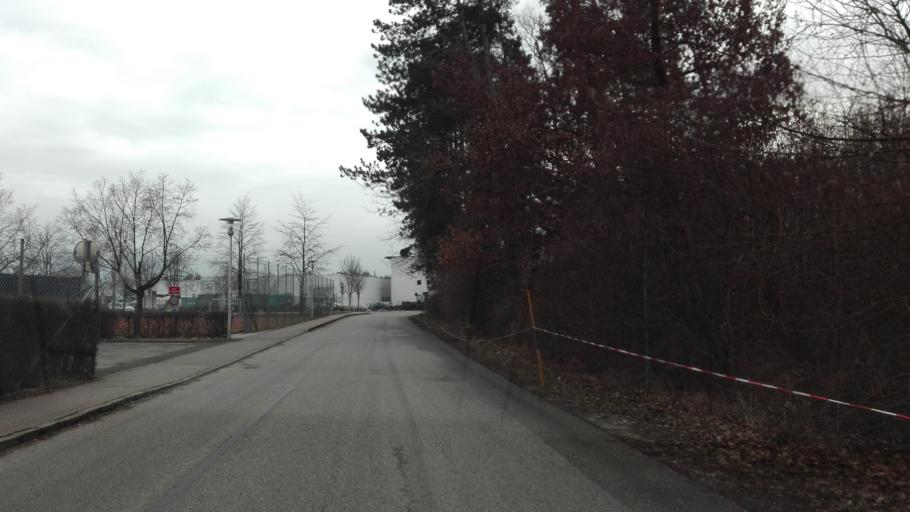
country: AT
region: Upper Austria
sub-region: Politischer Bezirk Linz-Land
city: Traun
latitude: 48.2355
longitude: 14.2266
